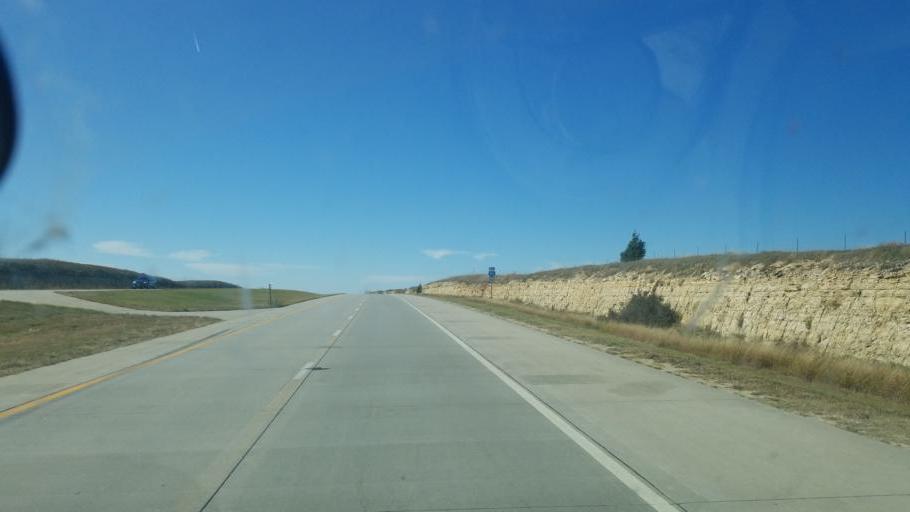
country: US
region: Kansas
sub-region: Riley County
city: Manhattan
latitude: 39.0663
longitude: -96.5819
